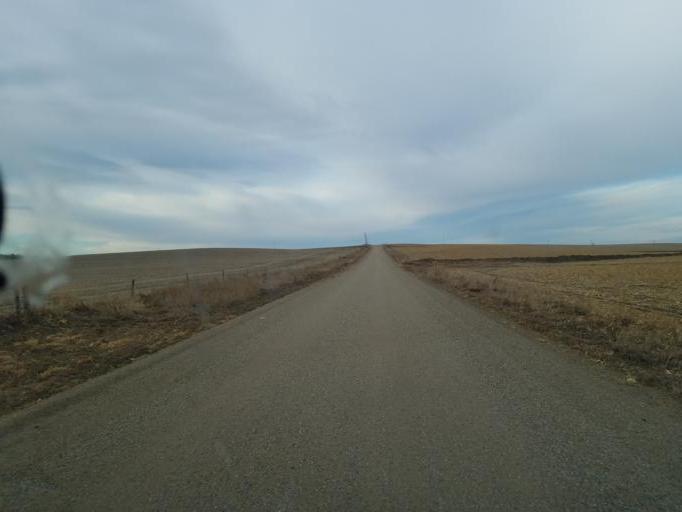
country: US
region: Nebraska
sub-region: Knox County
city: Bloomfield
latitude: 42.5833
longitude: -97.6764
